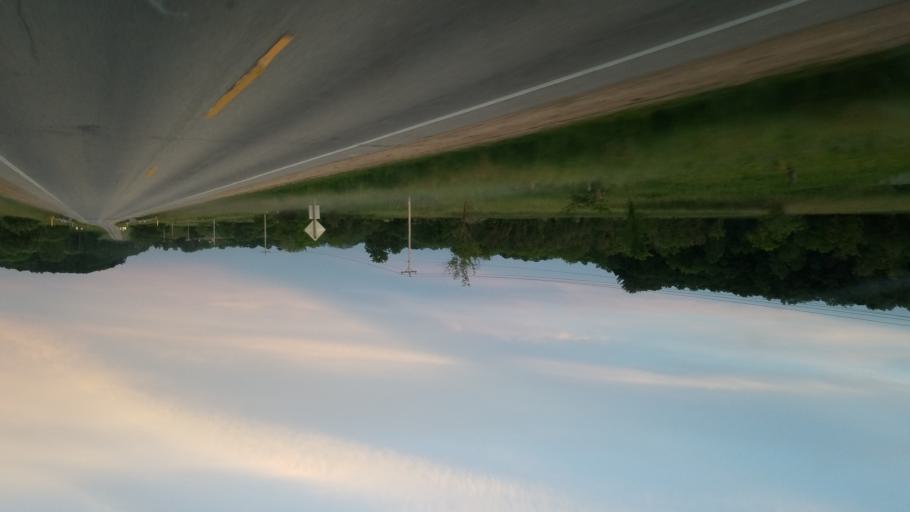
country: US
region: Wisconsin
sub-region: Juneau County
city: Elroy
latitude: 43.7876
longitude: -90.3586
